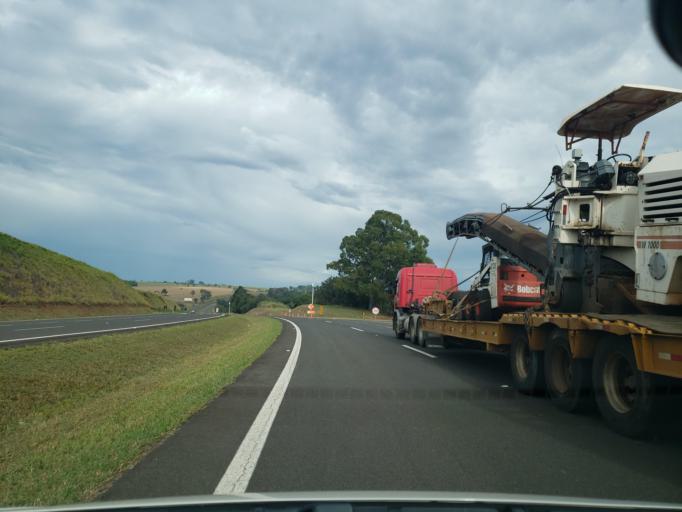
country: BR
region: Sao Paulo
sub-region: Dois Corregos
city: Dois Corregos
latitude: -22.2501
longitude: -48.3597
